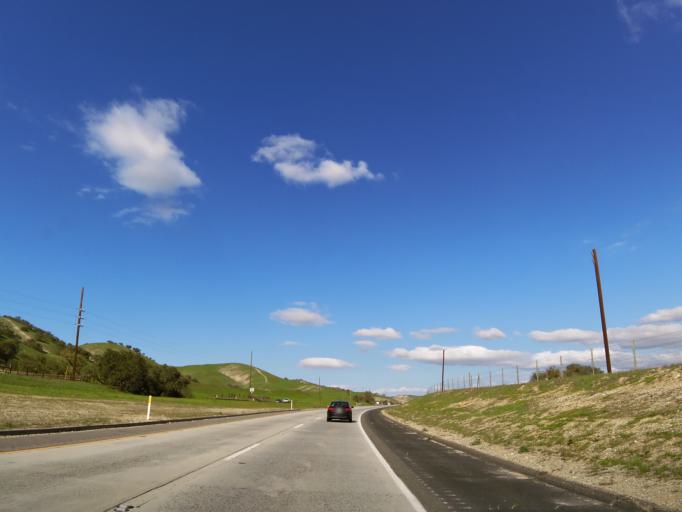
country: US
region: California
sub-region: San Luis Obispo County
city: Lake Nacimiento
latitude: 35.8842
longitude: -120.8415
